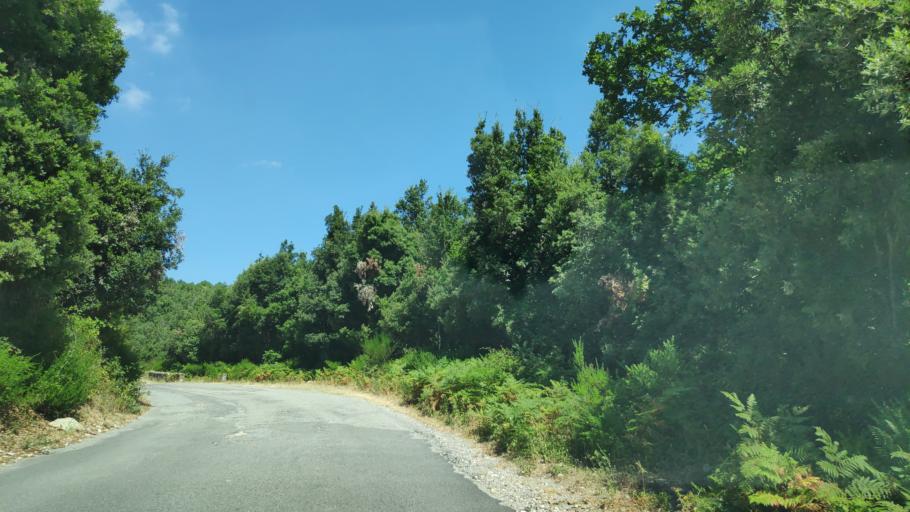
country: IT
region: Calabria
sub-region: Provincia di Reggio Calabria
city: Pazzano
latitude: 38.4722
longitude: 16.4077
